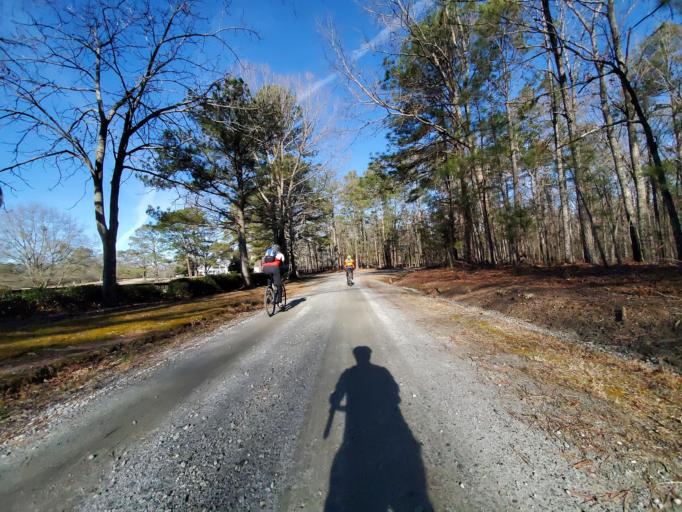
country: US
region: Georgia
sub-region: Fulton County
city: Chattahoochee Hills
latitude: 33.5621
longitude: -84.8072
